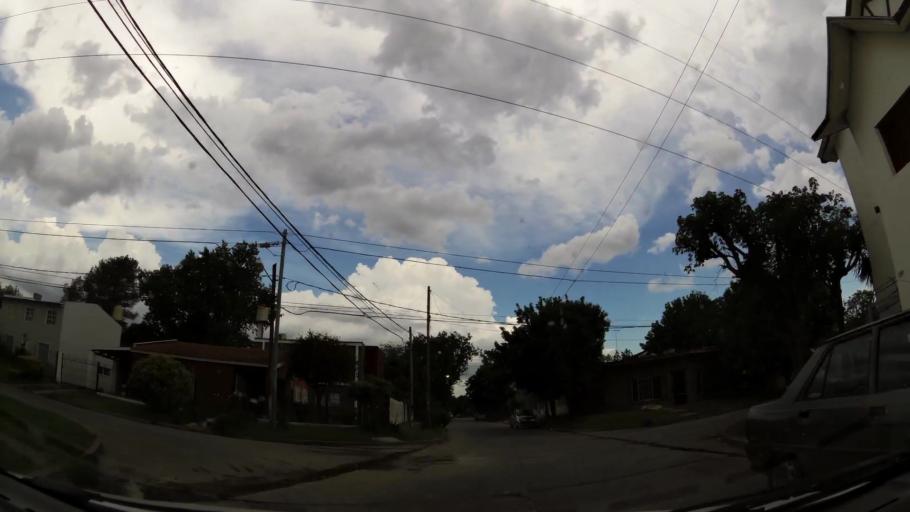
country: AR
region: Buenos Aires
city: Ituzaingo
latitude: -34.6392
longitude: -58.6832
